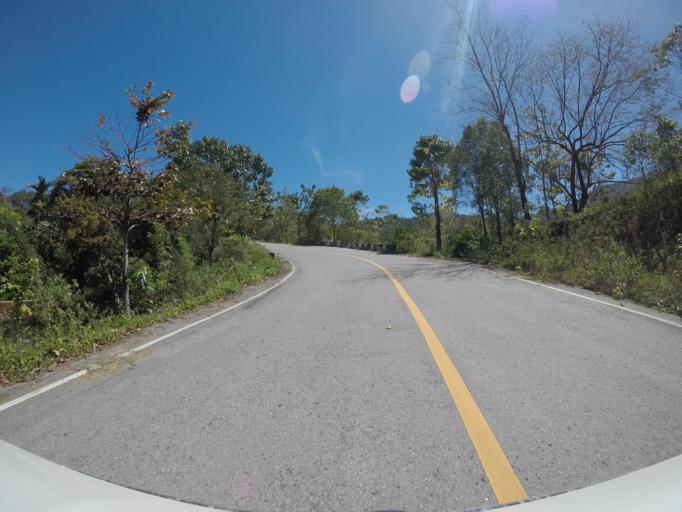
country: TL
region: Manatuto
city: Manatuto
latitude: -8.8178
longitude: 125.9750
